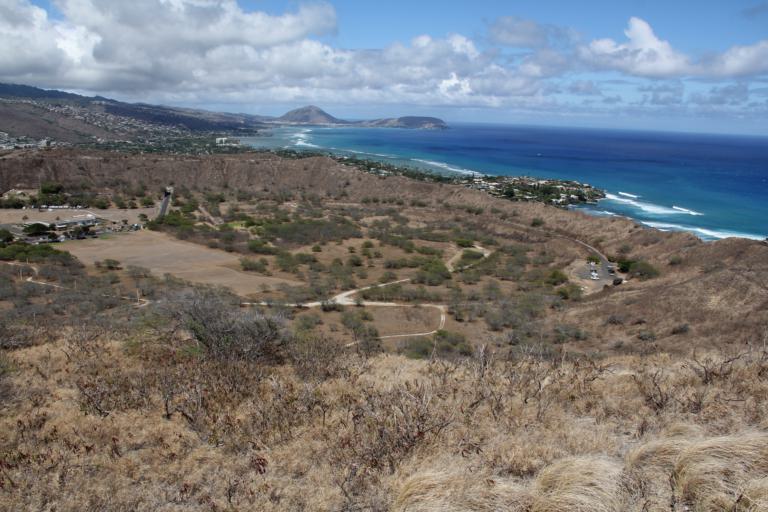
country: US
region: Hawaii
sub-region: Honolulu County
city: Honolulu
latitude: 21.2595
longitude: -157.8111
